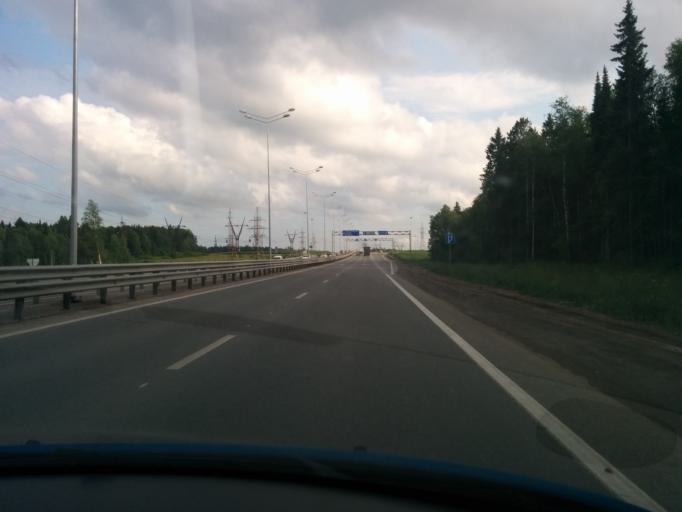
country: RU
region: Perm
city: Novyye Lyady
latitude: 58.0518
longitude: 56.4288
